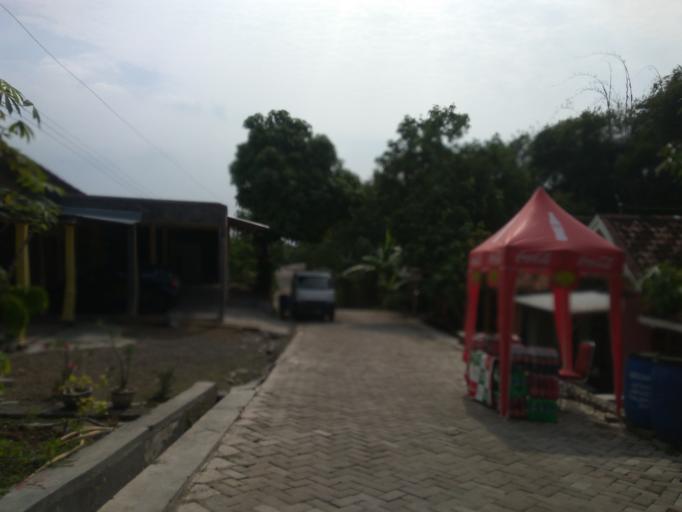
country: ID
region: Central Java
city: Semarang
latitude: -7.0352
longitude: 110.4094
